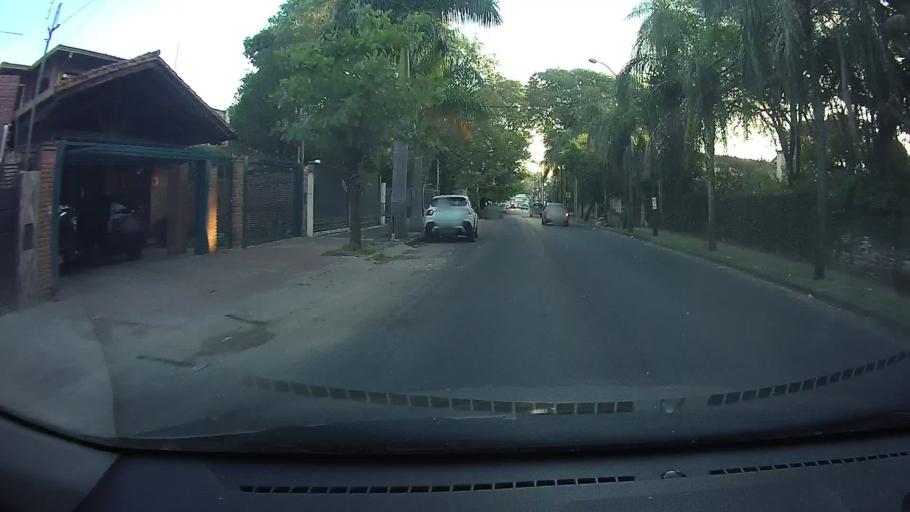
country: PY
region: Central
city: Lambare
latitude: -25.3123
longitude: -57.5797
